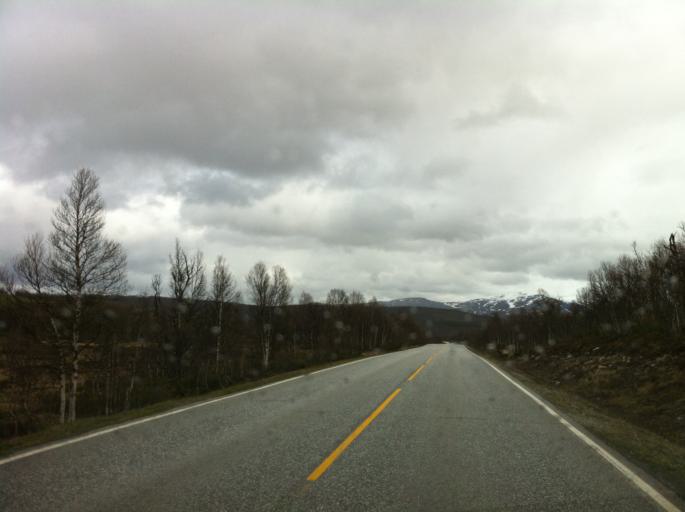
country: NO
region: Sor-Trondelag
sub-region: Roros
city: Roros
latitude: 62.6098
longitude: 11.6402
